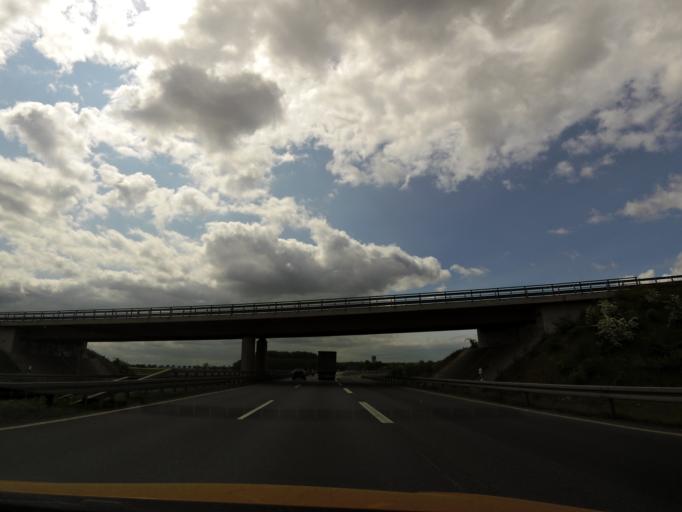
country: DE
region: Lower Saxony
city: Leiferde
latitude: 52.2107
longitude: 10.4910
